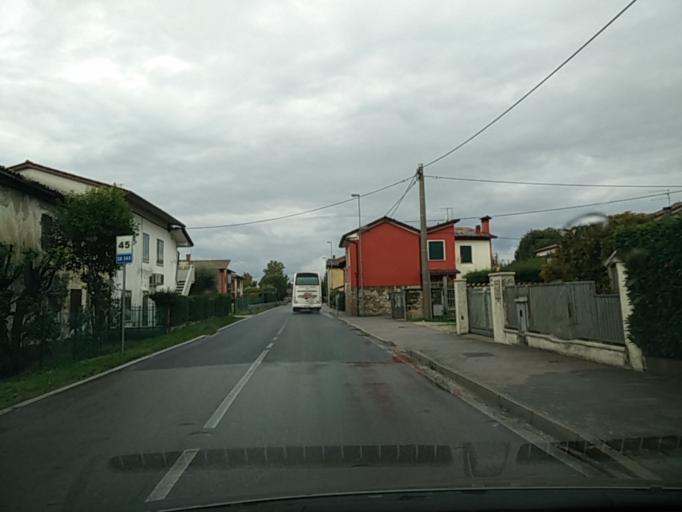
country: IT
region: Veneto
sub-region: Provincia di Vicenza
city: Rossano Veneto
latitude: 45.7038
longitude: 11.8132
